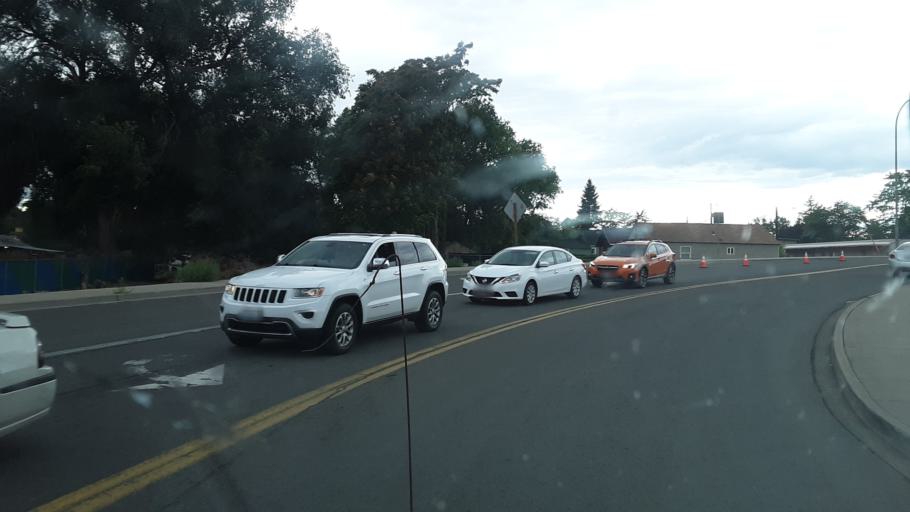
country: US
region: Washington
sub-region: Yakima County
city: Yakima
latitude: 46.6043
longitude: -120.4881
